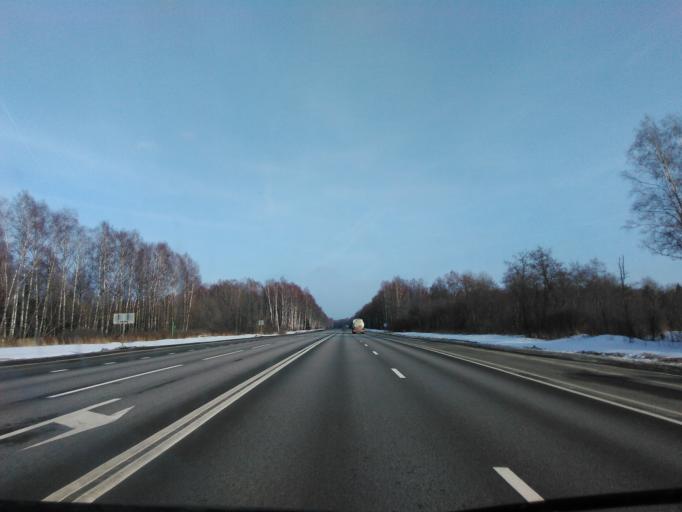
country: RU
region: Smolensk
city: Vyaz'ma
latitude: 55.1883
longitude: 34.0379
